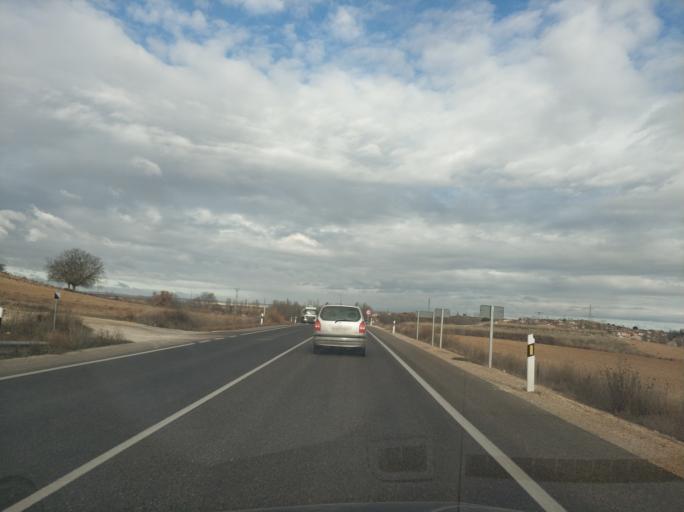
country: ES
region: Castille and Leon
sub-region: Provincia de Burgos
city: Castrillo de la Vega
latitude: 41.6448
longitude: -3.7804
